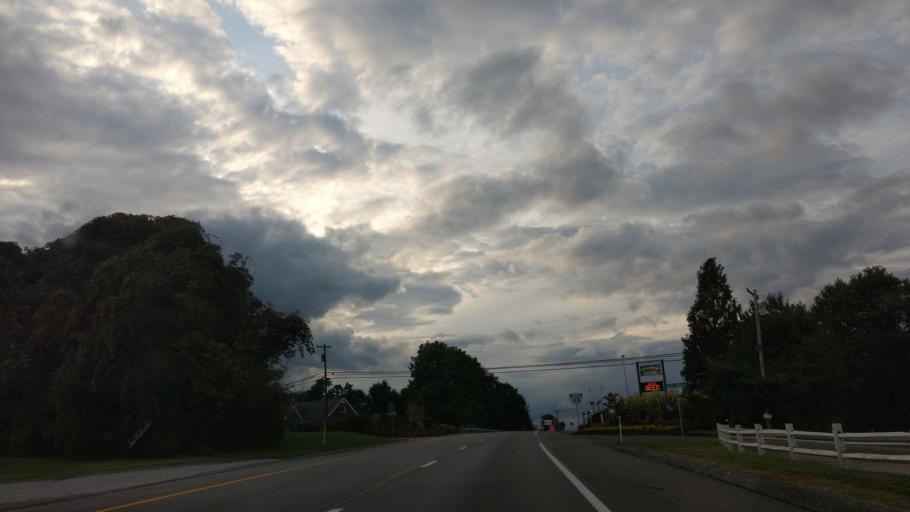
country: US
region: Pennsylvania
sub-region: Westmoreland County
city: Fellsburg
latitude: 40.2010
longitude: -79.8339
